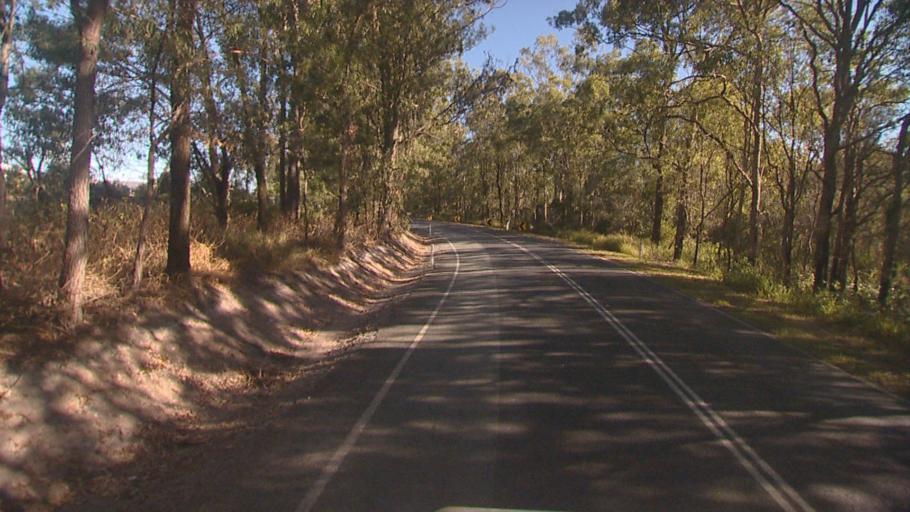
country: AU
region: Queensland
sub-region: Logan
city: Logan Reserve
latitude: -27.7485
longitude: 153.1318
